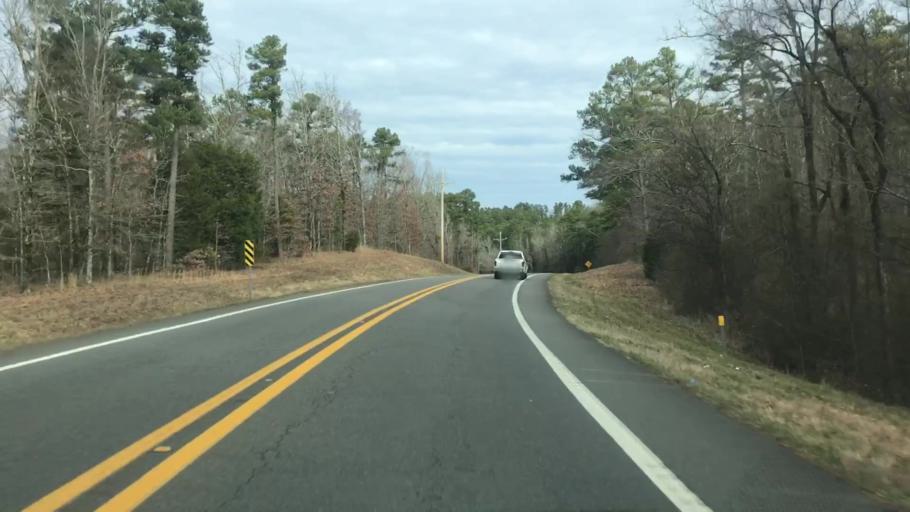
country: US
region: Arkansas
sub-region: Montgomery County
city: Mount Ida
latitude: 34.5891
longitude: -93.6640
